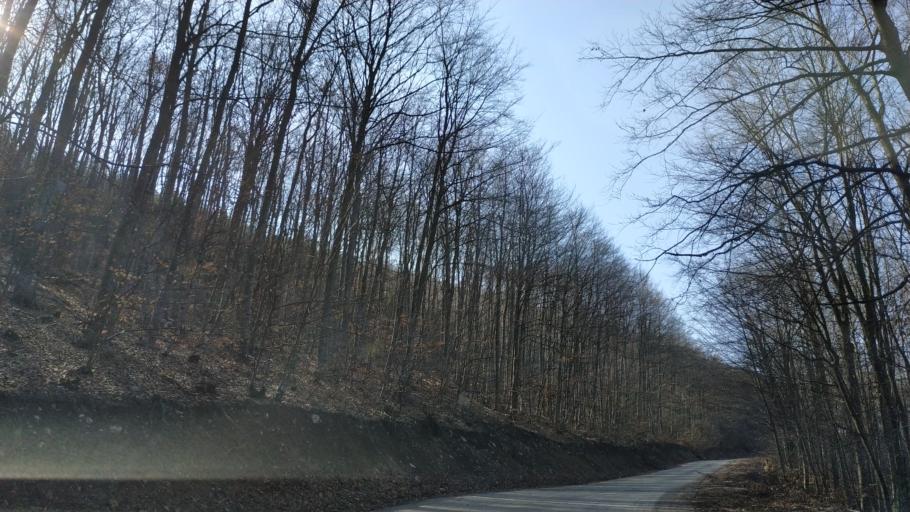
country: RS
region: Central Serbia
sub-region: Zajecarski Okrug
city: Soko Banja
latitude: 43.5973
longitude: 21.8904
